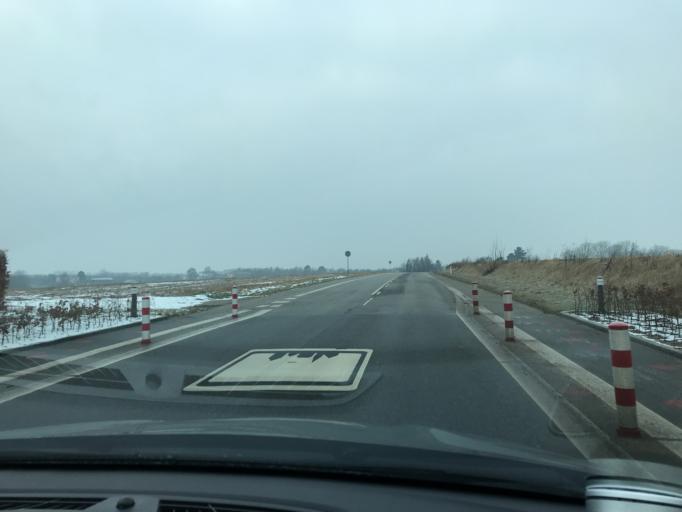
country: DK
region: Zealand
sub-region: Odsherred Kommune
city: Horve
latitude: 55.7584
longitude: 11.4482
